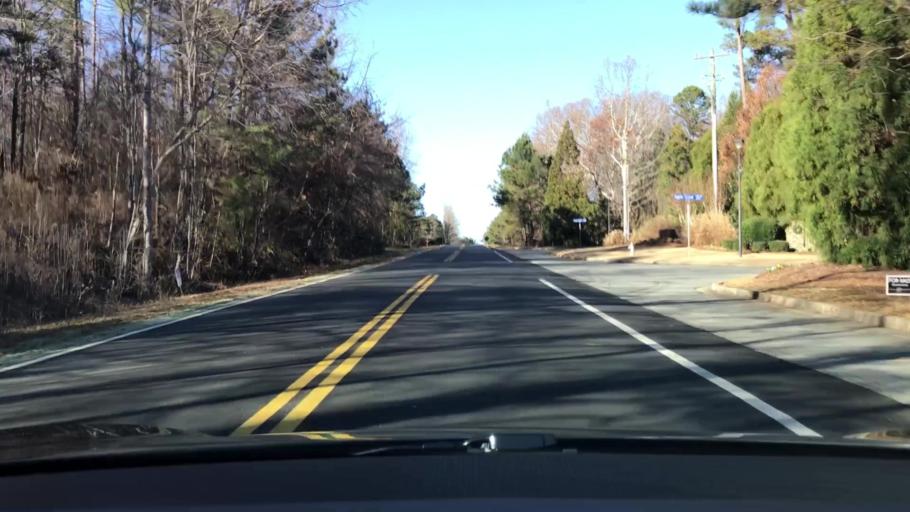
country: US
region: Georgia
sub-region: Barrow County
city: Auburn
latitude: 34.0859
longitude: -83.8686
